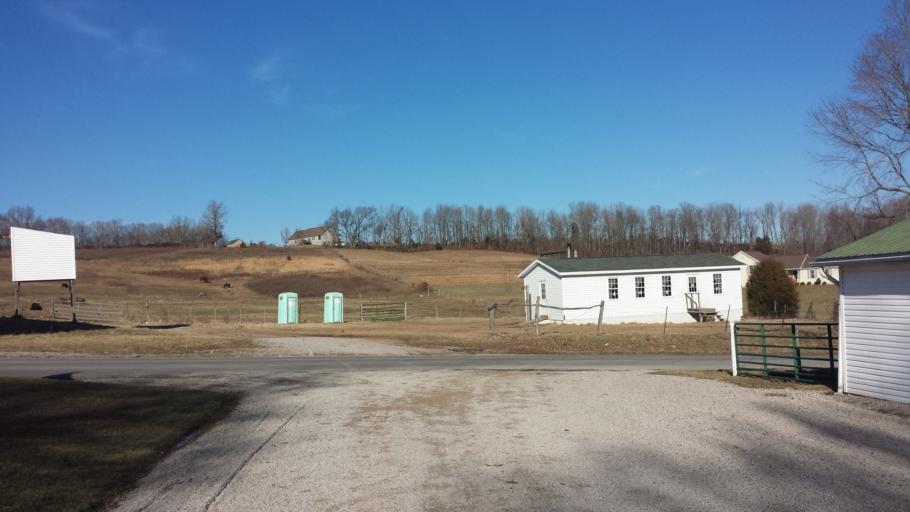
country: US
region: Ohio
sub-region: Jackson County
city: Oak Hill
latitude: 38.8279
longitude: -82.4023
